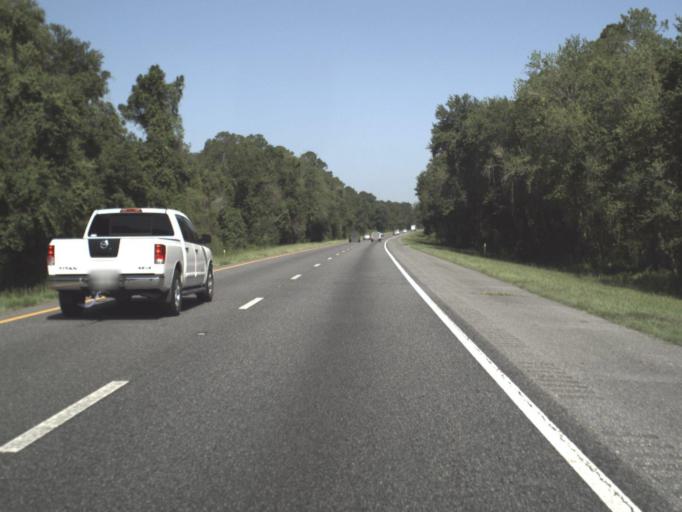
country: US
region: Florida
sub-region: Suwannee County
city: Live Oak
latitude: 30.2995
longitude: -82.9062
